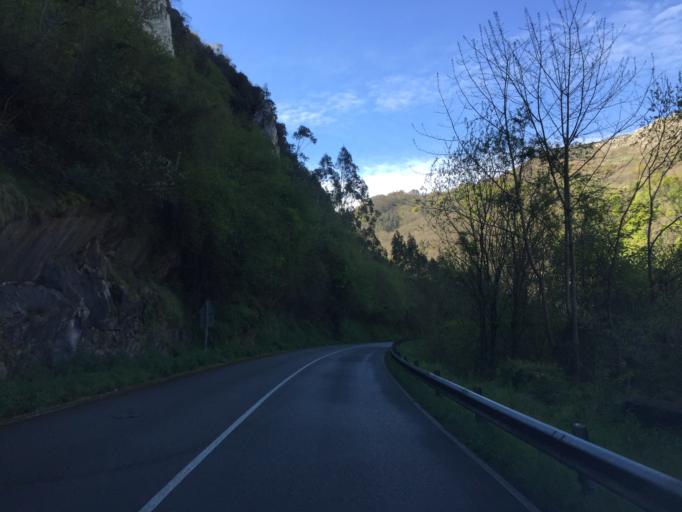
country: ES
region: Asturias
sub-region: Province of Asturias
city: Proaza
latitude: 43.3038
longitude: -5.9841
